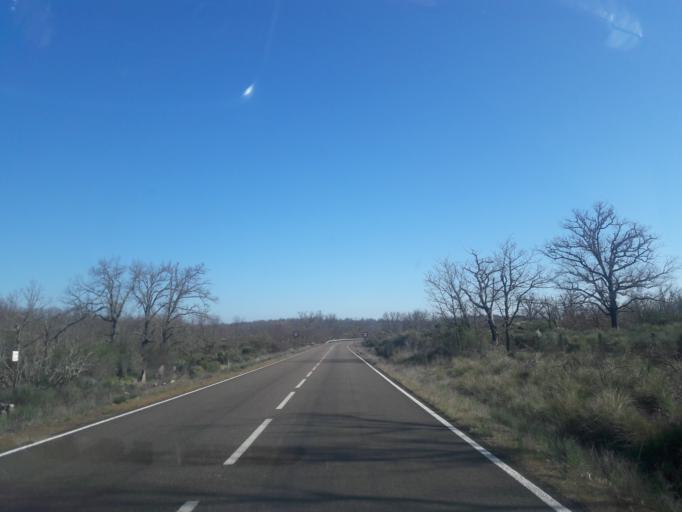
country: ES
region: Castille and Leon
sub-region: Provincia de Salamanca
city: Cabeza del Caballo
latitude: 41.0896
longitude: -6.5580
